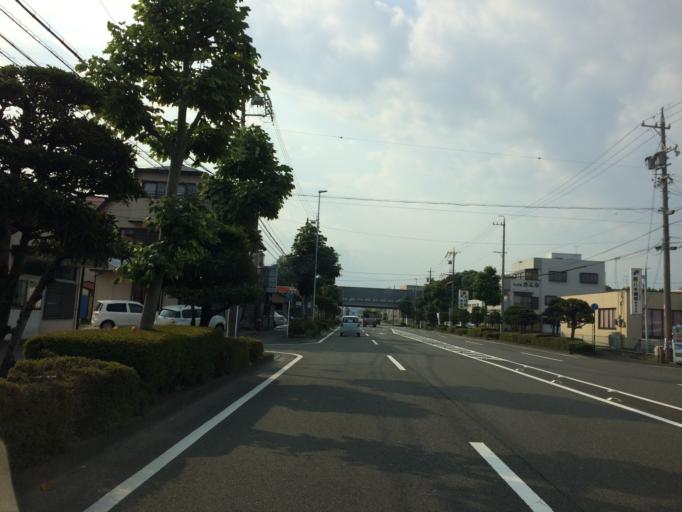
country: JP
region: Shizuoka
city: Shizuoka-shi
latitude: 34.9569
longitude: 138.4181
